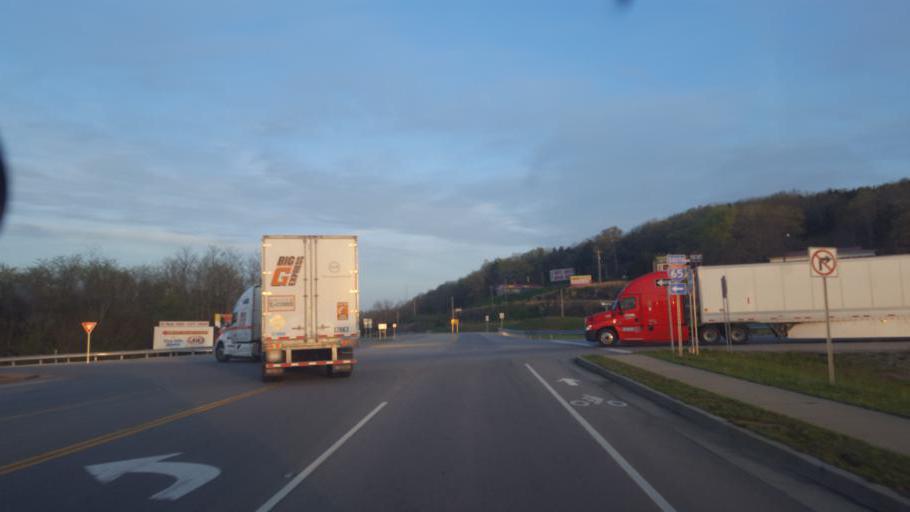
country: US
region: Kentucky
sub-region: Barren County
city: Cave City
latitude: 37.1357
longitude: -85.9785
